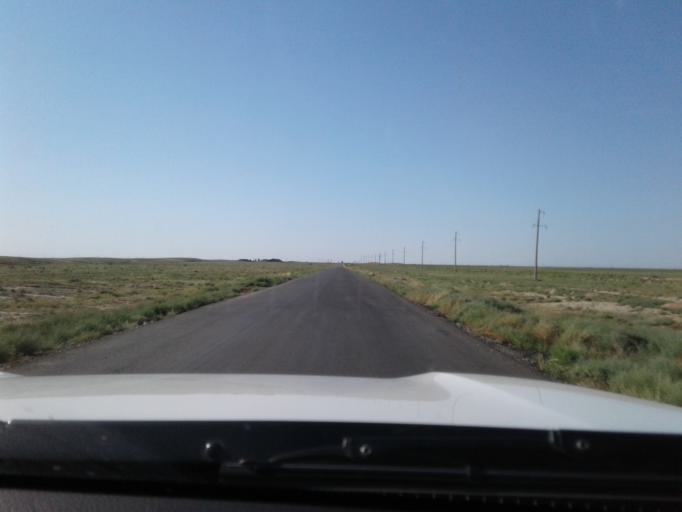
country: IR
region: Razavi Khorasan
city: Kalat-e Naderi
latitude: 37.1639
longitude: 60.0491
